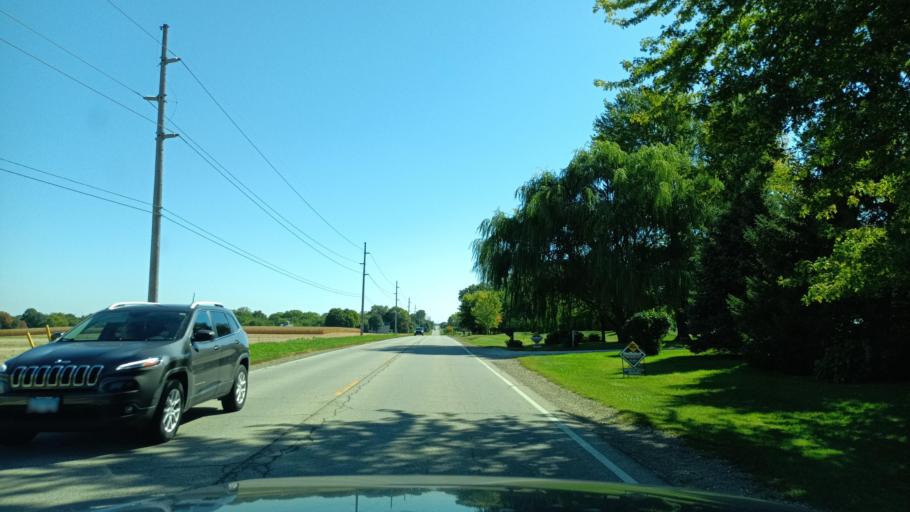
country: US
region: Illinois
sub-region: Peoria County
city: Dunlap
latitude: 40.7855
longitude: -89.7247
